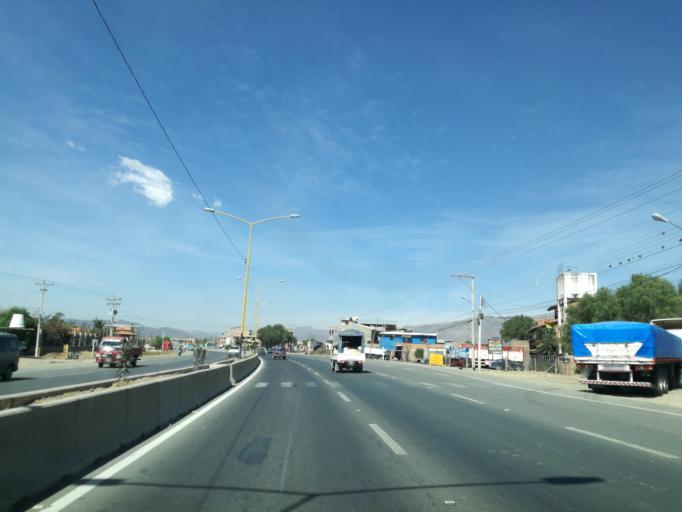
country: BO
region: Cochabamba
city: Sipe Sipe
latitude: -17.4130
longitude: -66.3334
